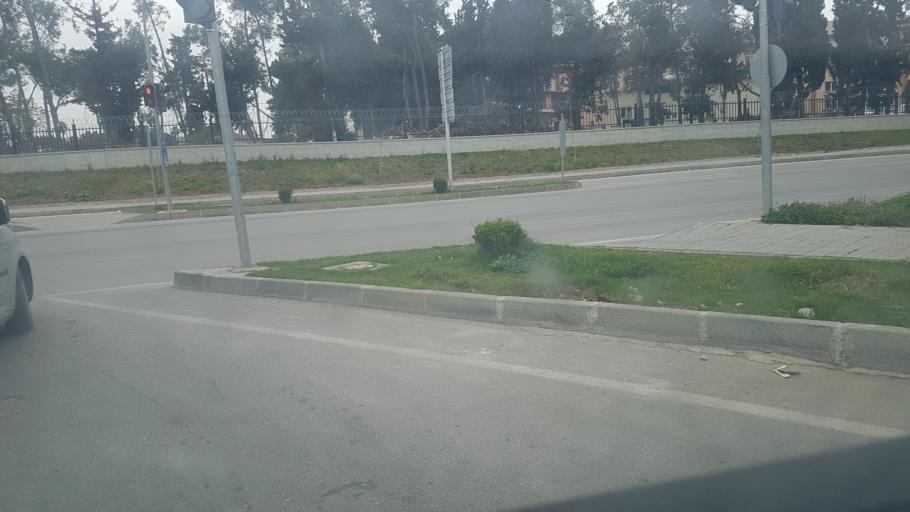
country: TR
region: Adana
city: Adana
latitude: 37.0139
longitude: 35.3386
